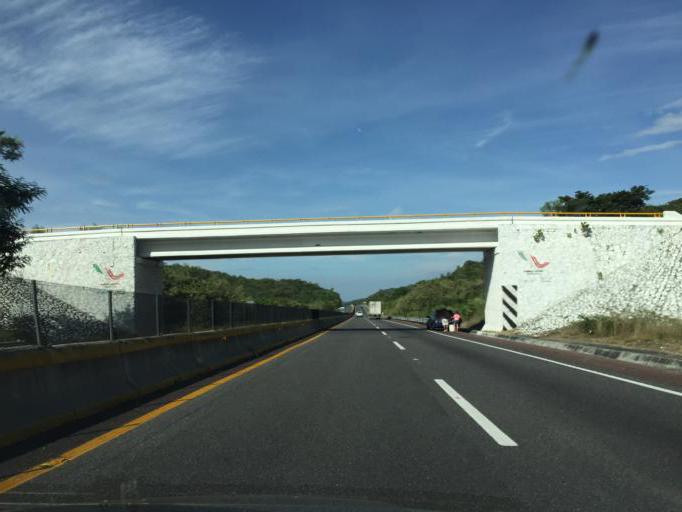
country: MX
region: Guerrero
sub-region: Huitzuco de los Figueroa
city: Ciudad de Huitzuco
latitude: 18.2871
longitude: -99.2086
